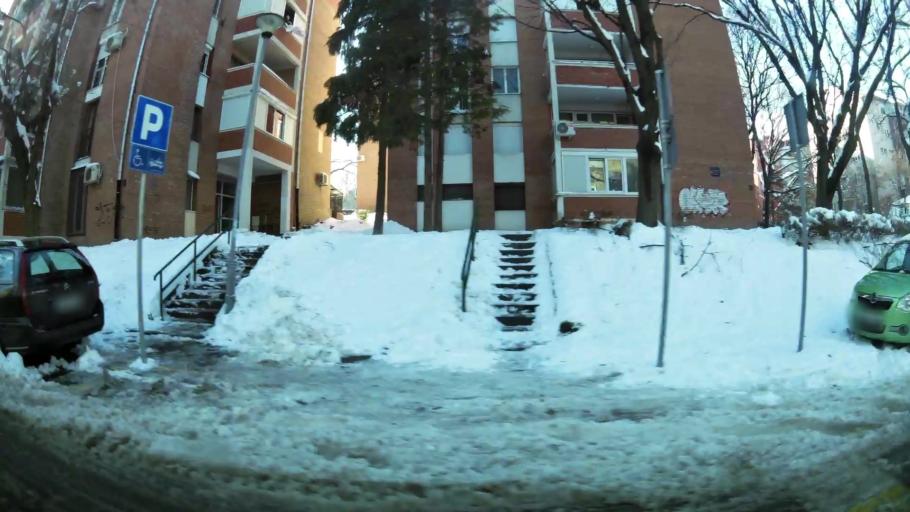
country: RS
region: Central Serbia
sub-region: Belgrade
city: Palilula
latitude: 44.8128
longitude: 20.5100
